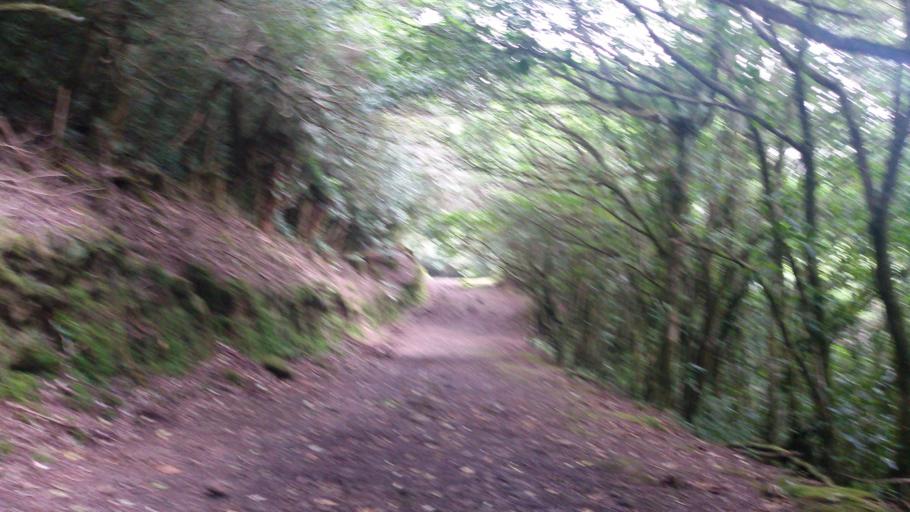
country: CR
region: Heredia
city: Angeles
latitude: 10.0495
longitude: -84.0202
